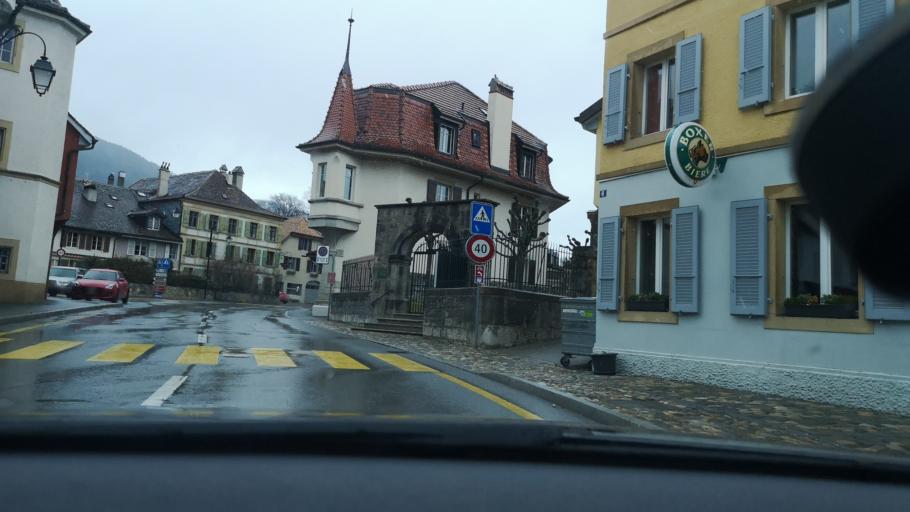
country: CH
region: Neuchatel
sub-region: Boudry District
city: Bevaix
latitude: 46.9304
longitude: 6.8154
